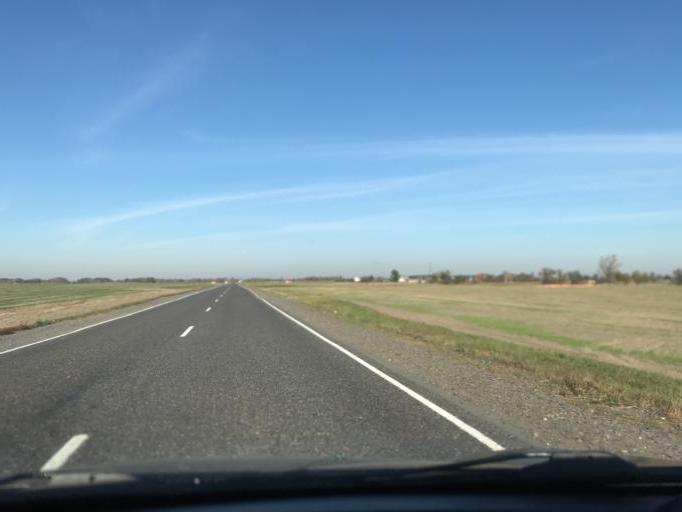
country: BY
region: Gomel
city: Brahin
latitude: 51.6620
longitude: 30.4288
